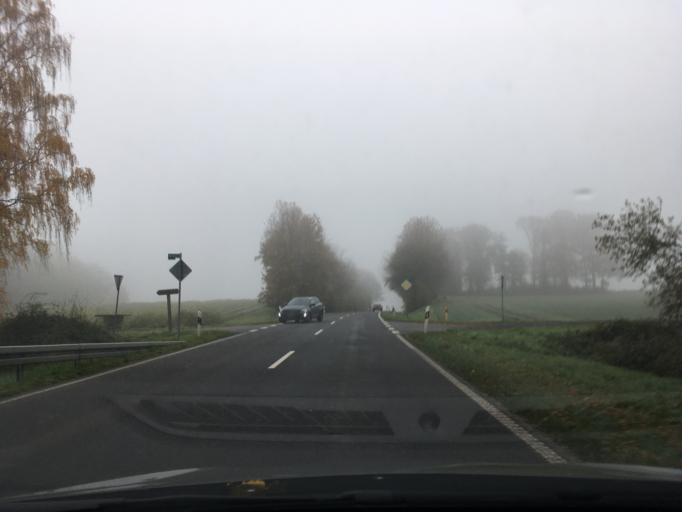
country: DE
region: North Rhine-Westphalia
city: Stadtlohn
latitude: 52.0567
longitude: 6.9405
